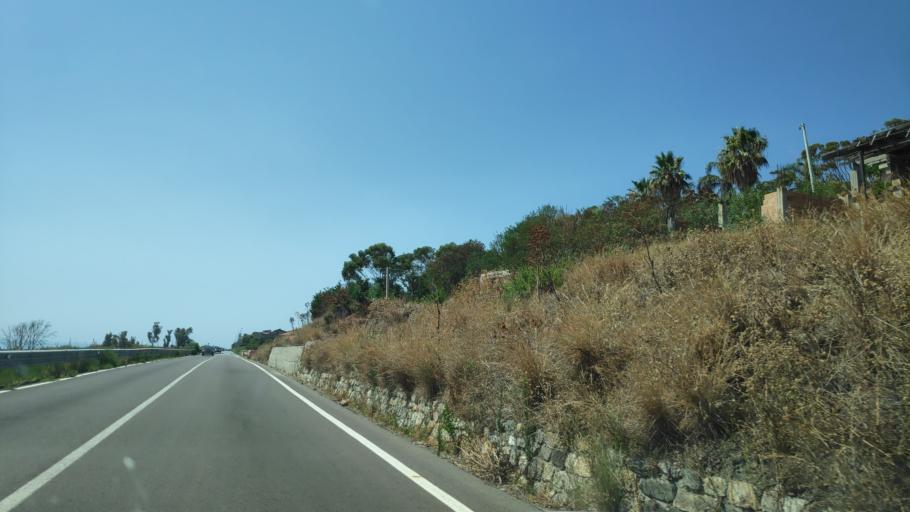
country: IT
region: Calabria
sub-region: Provincia di Reggio Calabria
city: Brancaleone-Marina
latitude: 37.9968
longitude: 16.1225
